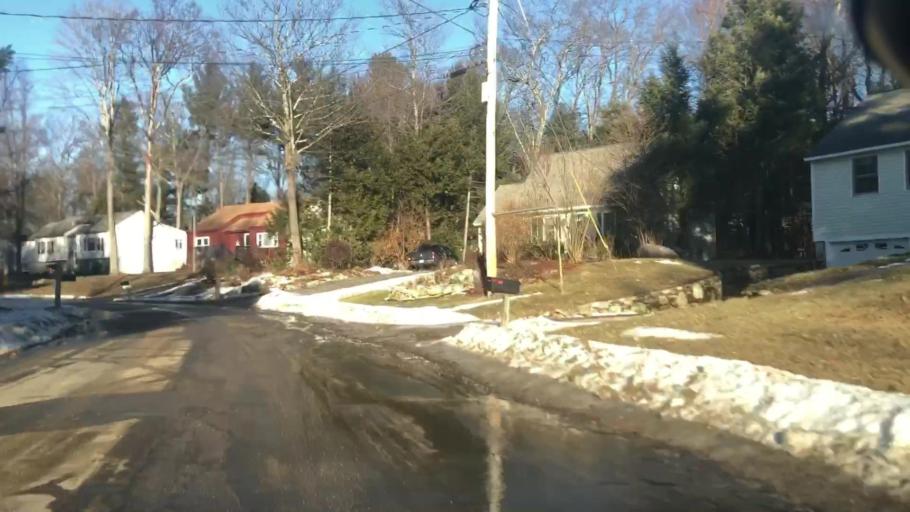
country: US
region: New Hampshire
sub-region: Hillsborough County
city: Milford
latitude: 42.8321
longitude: -71.6735
